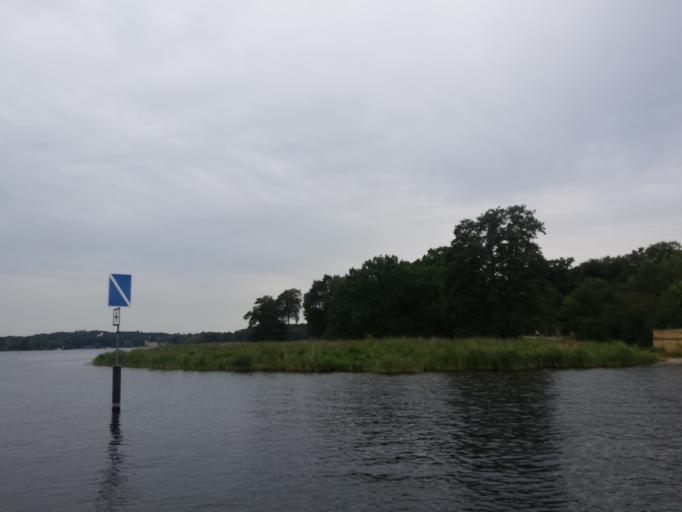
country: DE
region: Brandenburg
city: Potsdam
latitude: 52.4240
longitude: 13.0971
